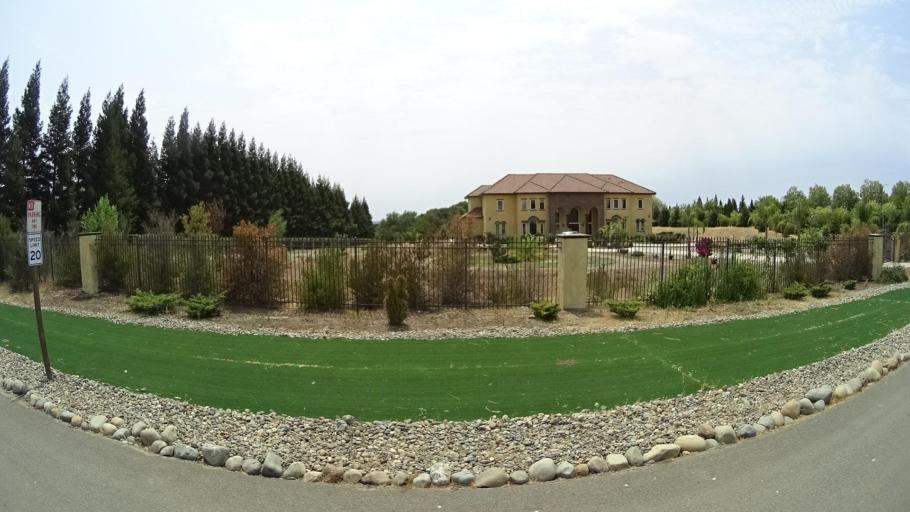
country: US
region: California
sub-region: Placer County
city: Rocklin
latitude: 38.7720
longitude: -121.2130
